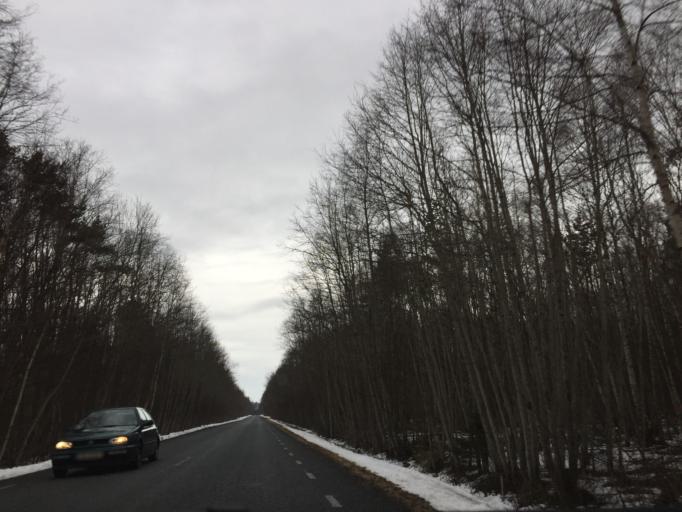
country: EE
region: Saare
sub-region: Orissaare vald
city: Orissaare
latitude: 58.5618
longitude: 22.7718
